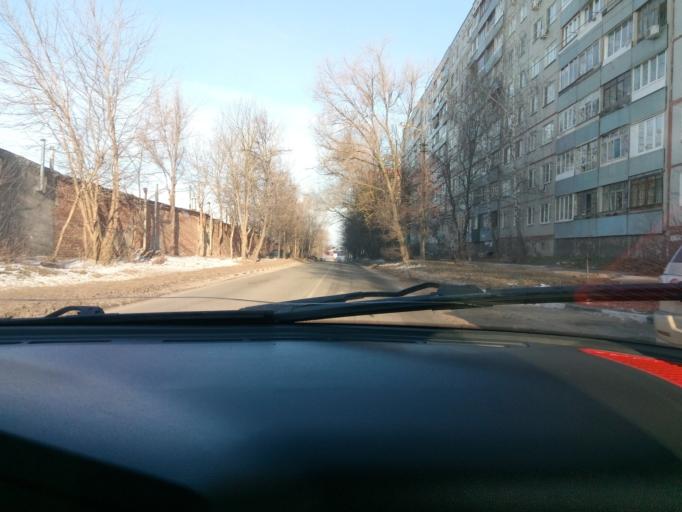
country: RU
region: Tula
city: Mendeleyevskiy
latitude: 54.1652
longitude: 37.5610
